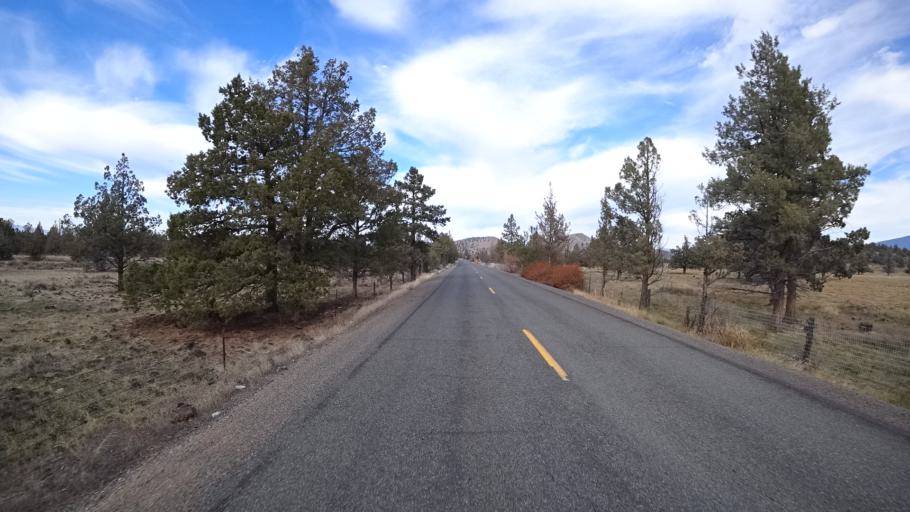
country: US
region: California
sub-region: Siskiyou County
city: Montague
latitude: 41.6357
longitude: -122.4383
